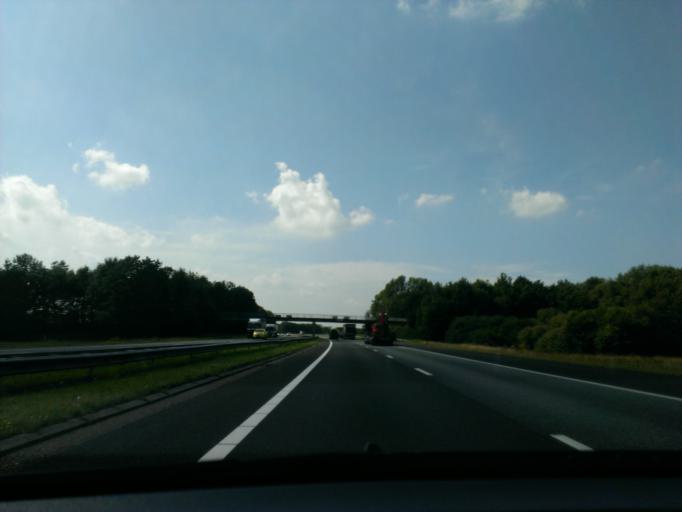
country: NL
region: Drenthe
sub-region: Gemeente Meppel
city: Meppel
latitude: 52.6859
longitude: 6.2389
